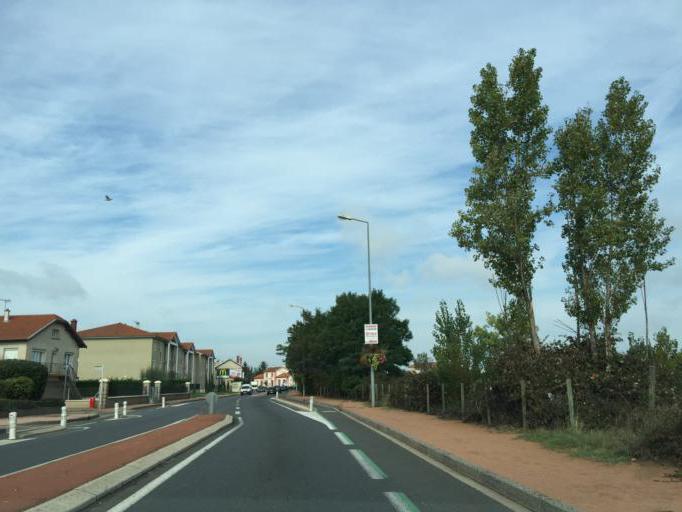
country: FR
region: Rhone-Alpes
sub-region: Departement de la Loire
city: Bonson
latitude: 45.5208
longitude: 4.2191
